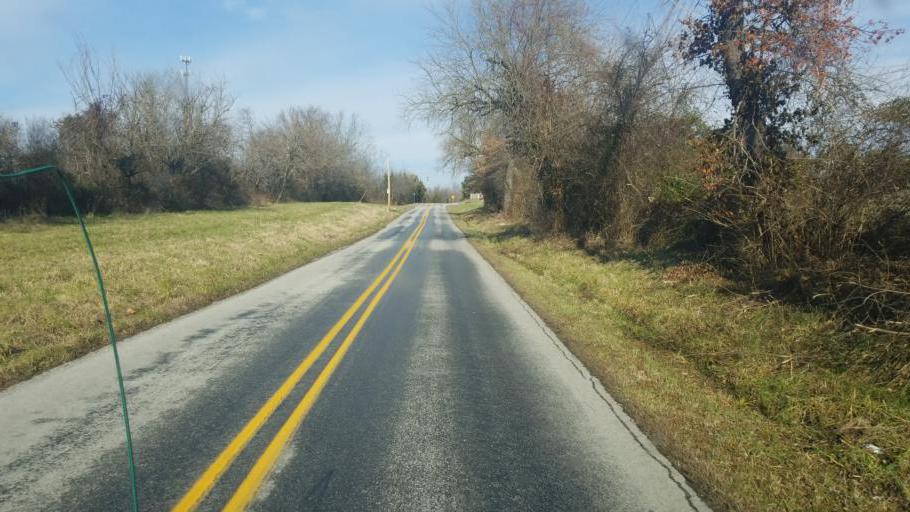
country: US
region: Illinois
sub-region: Jackson County
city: Carbondale
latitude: 37.6967
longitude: -89.2119
